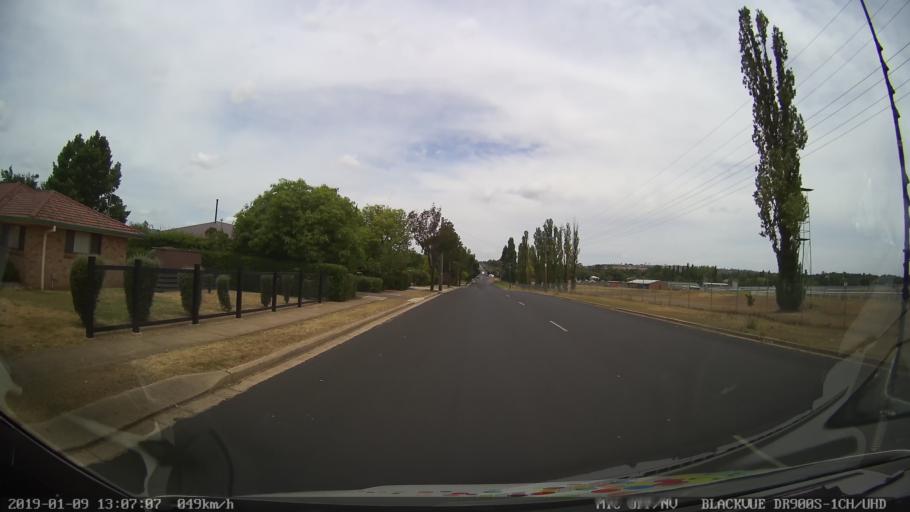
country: AU
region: New South Wales
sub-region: Armidale Dumaresq
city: Armidale
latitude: -30.5173
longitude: 151.6805
